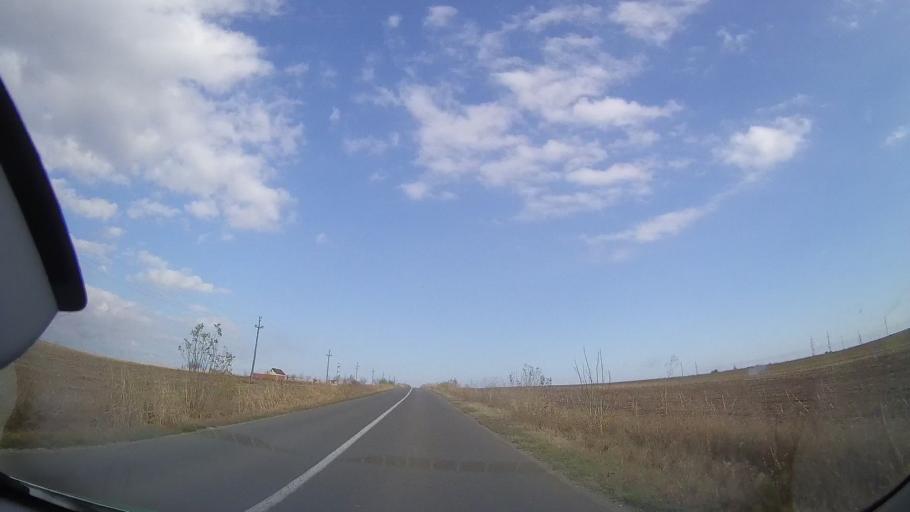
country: RO
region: Constanta
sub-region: Comuna Douazeci si Trei August
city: Dulcesti
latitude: 43.8995
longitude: 28.5299
